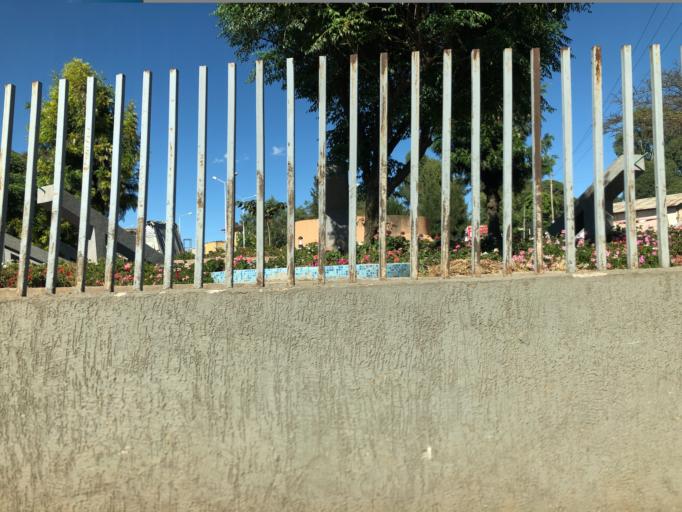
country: ET
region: Amhara
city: Gondar
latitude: 12.6179
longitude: 37.4704
